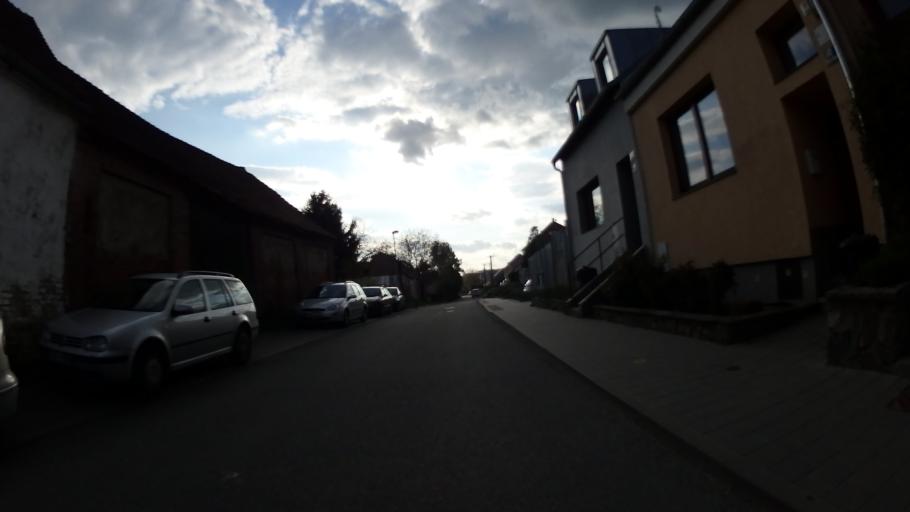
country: CZ
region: South Moravian
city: Ostopovice
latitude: 49.1654
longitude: 16.5634
